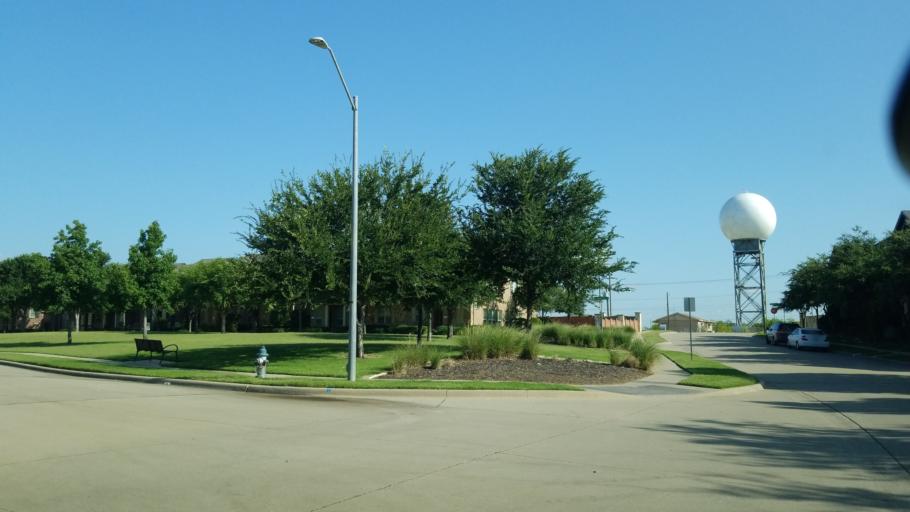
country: US
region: Texas
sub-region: Dallas County
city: Coppell
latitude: 32.9243
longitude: -96.9680
